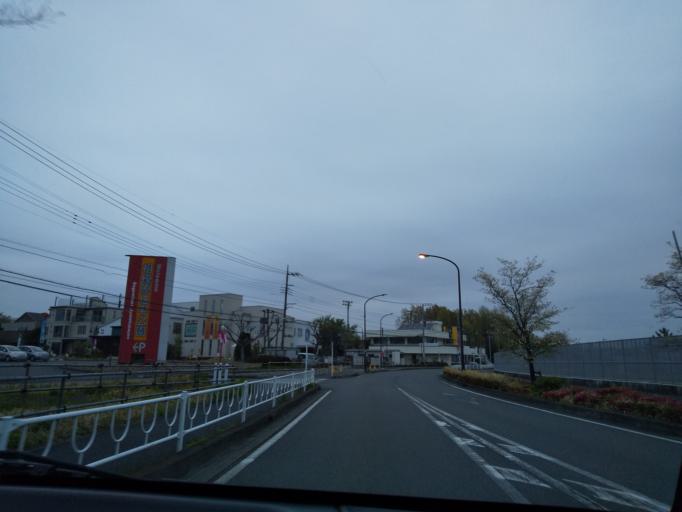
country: JP
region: Tokyo
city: Hachioji
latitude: 35.5842
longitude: 139.3673
